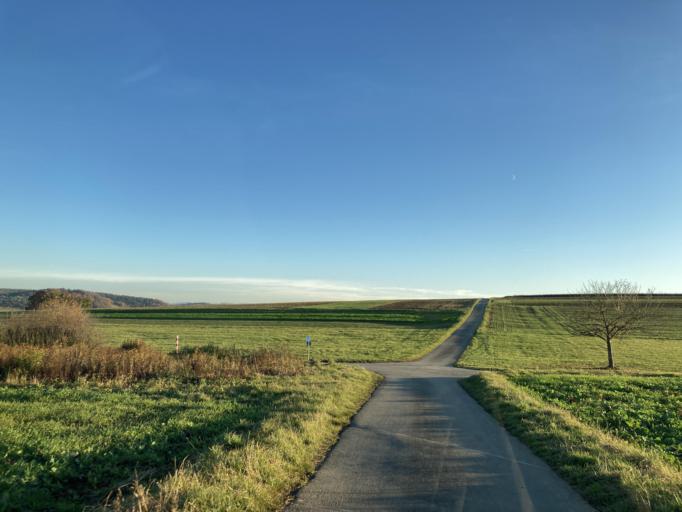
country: DE
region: Baden-Wuerttemberg
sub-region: Tuebingen Region
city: Hirrlingen
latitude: 48.4327
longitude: 8.9030
